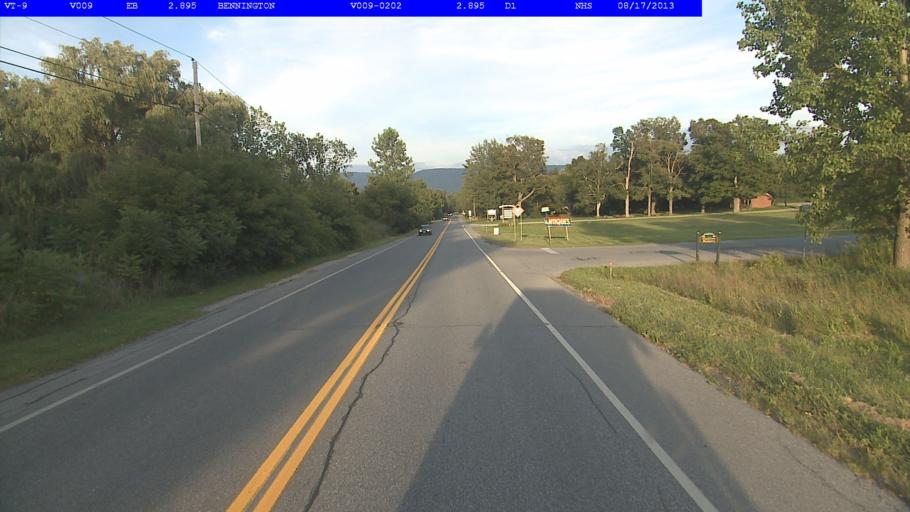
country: US
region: Vermont
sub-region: Bennington County
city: Bennington
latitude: 42.8821
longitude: -73.2225
